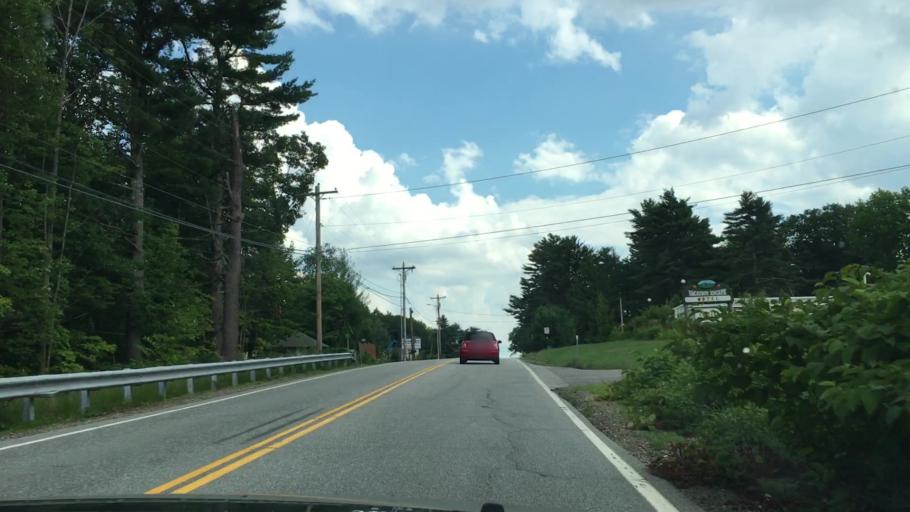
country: US
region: New Hampshire
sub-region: Belknap County
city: Meredith
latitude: 43.6266
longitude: -71.4868
